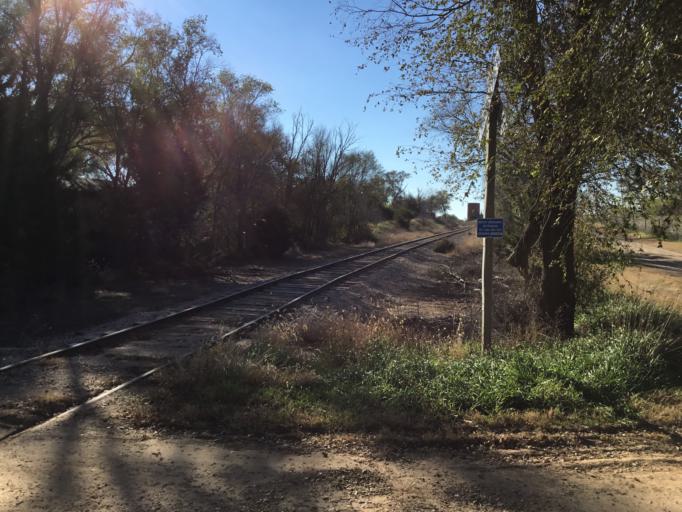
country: US
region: Kansas
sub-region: Lincoln County
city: Lincoln
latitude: 39.0337
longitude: -98.1527
